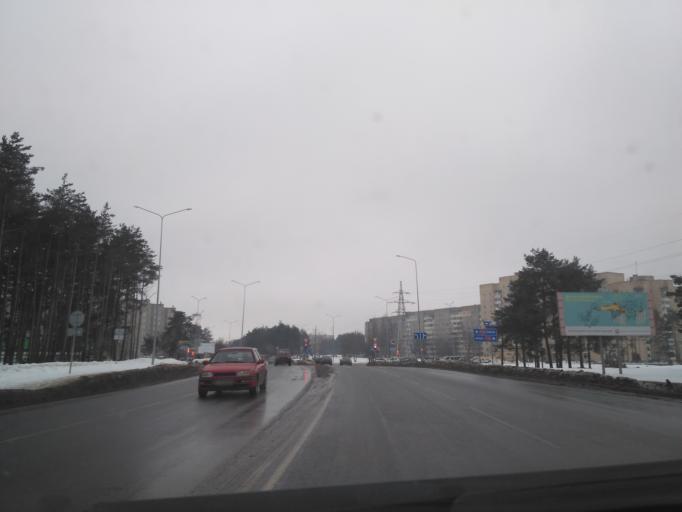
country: BY
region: Minsk
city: Horad Barysaw
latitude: 54.2021
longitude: 28.4834
